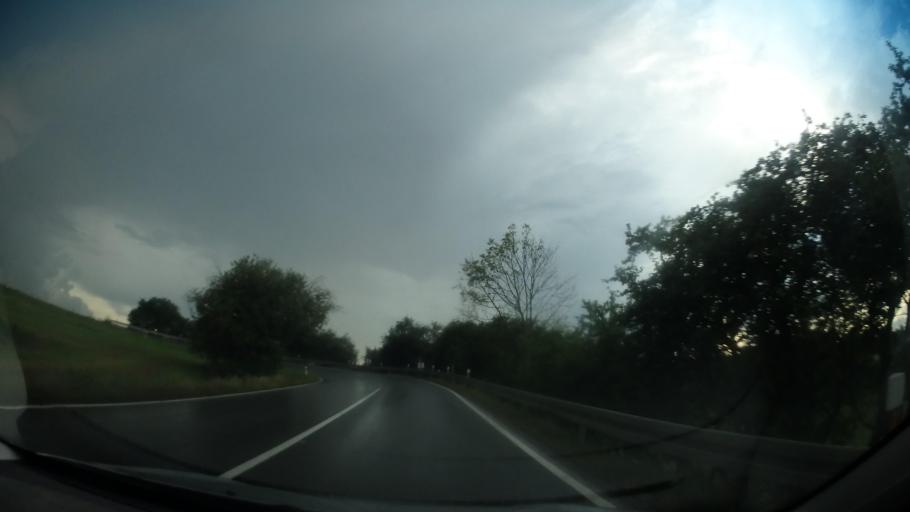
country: CZ
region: Olomoucky
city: Bila Lhota
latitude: 49.7092
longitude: 16.9816
